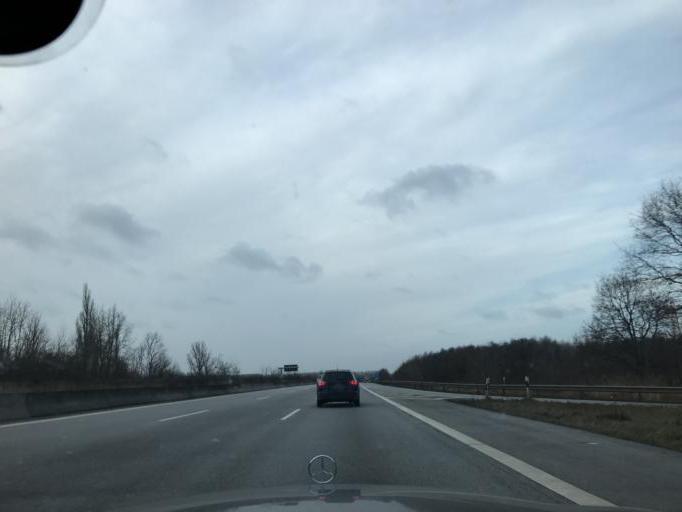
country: DE
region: Schleswig-Holstein
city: Oststeinbek
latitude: 53.5248
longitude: 10.1298
